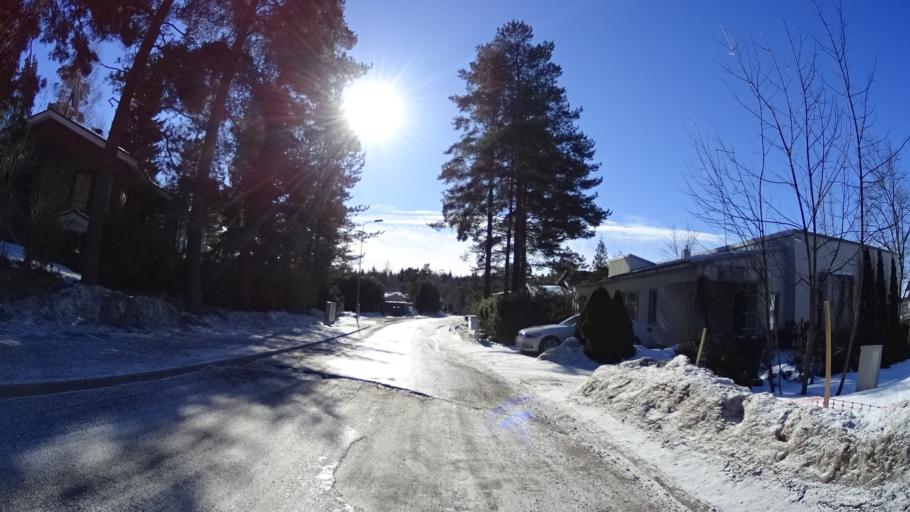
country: FI
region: Uusimaa
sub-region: Helsinki
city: Kauniainen
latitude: 60.1911
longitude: 24.7521
